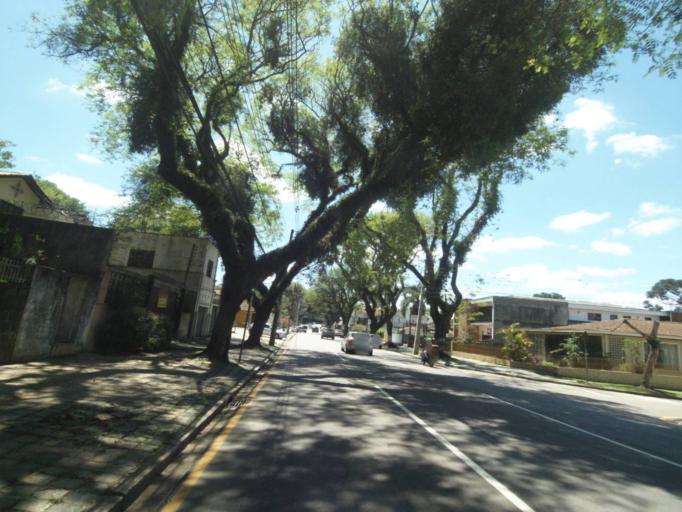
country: BR
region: Parana
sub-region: Curitiba
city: Curitiba
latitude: -25.3999
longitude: -49.2715
